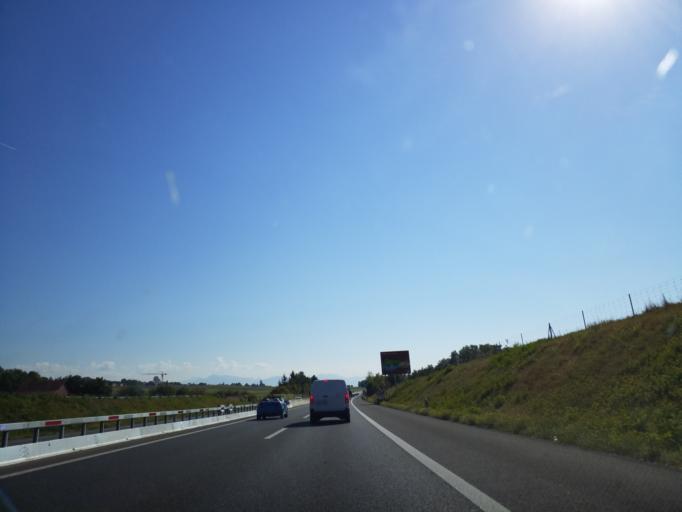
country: CH
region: Vaud
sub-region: Gros-de-Vaud District
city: Penthalaz
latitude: 46.6211
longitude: 6.5599
